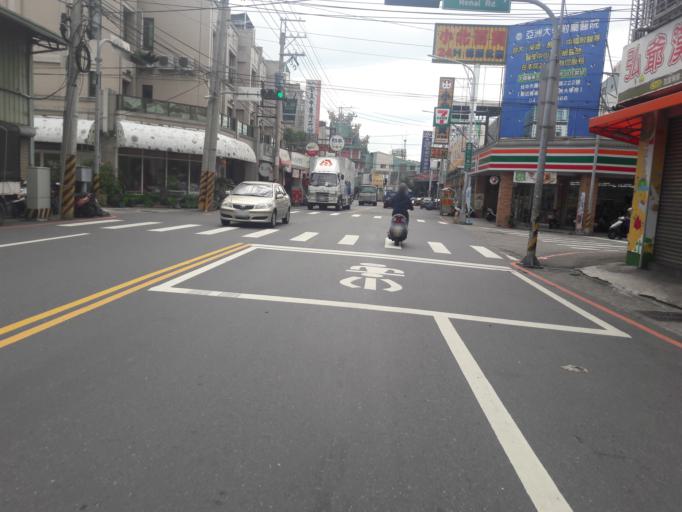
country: TW
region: Taiwan
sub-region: Taichung City
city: Taichung
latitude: 24.0960
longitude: 120.7038
